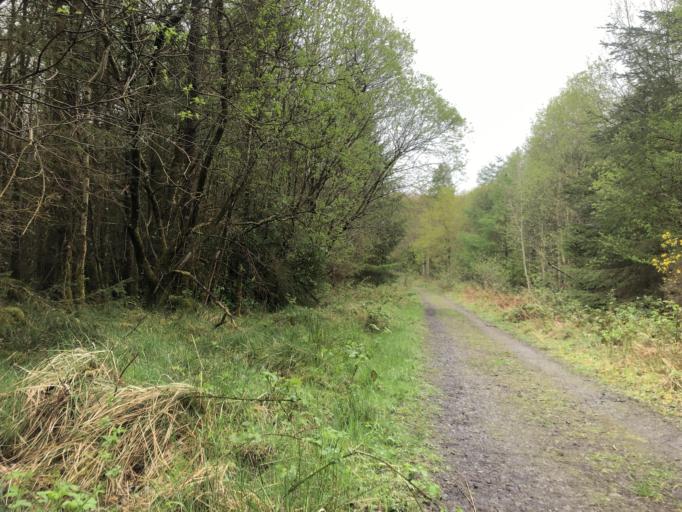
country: IE
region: Connaught
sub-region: Roscommon
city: Boyle
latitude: 53.9879
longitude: -8.1947
